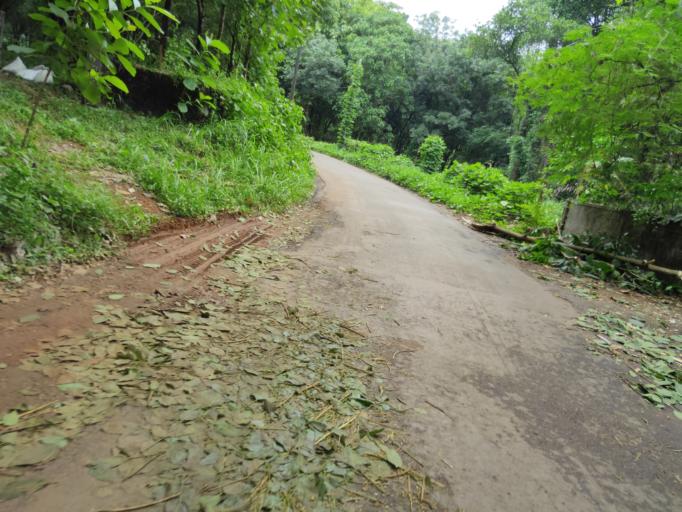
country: IN
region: Kerala
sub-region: Malappuram
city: Manjeri
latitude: 11.2208
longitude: 76.2519
